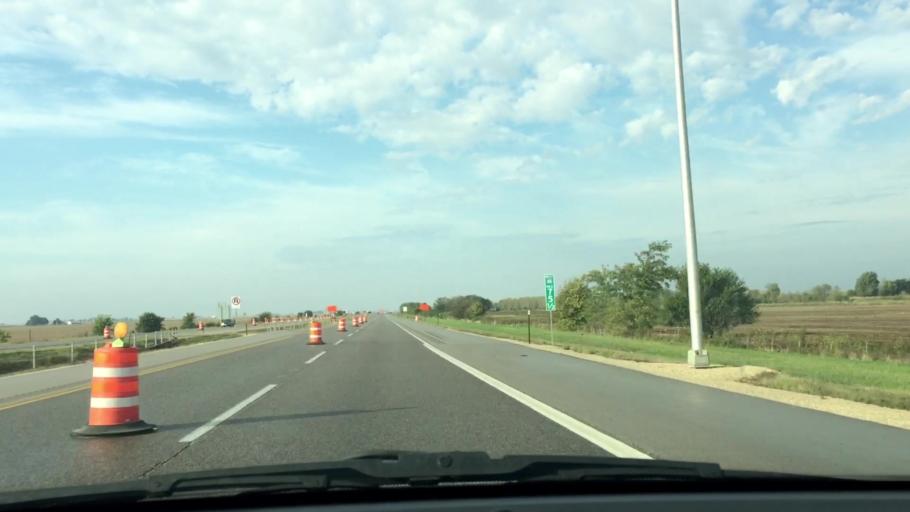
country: US
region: Illinois
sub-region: Ogle County
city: Rochelle
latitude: 41.8973
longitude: -89.0801
